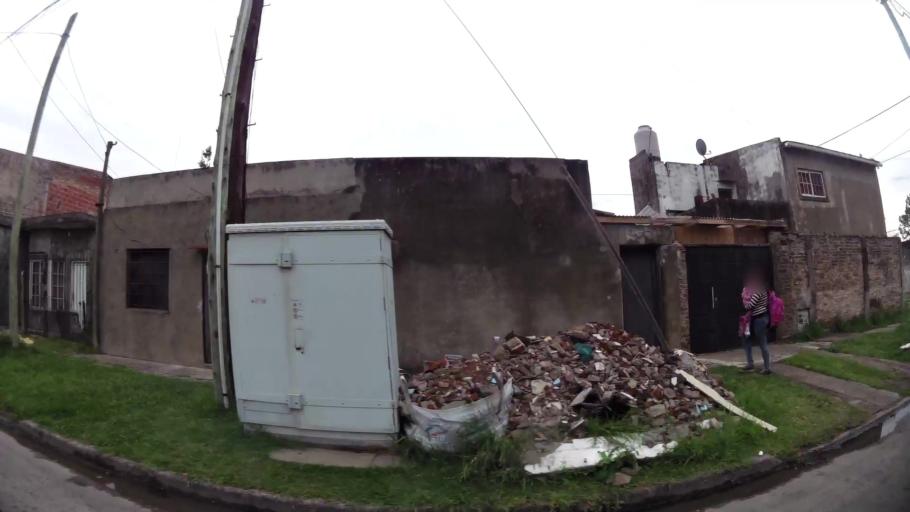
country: AR
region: Buenos Aires
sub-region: Partido de Lanus
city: Lanus
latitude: -34.7012
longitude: -58.3686
